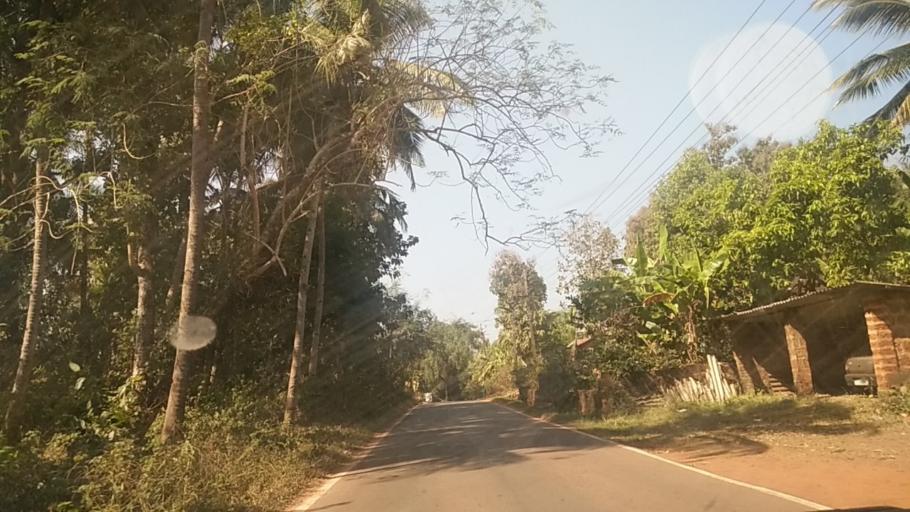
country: IN
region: Goa
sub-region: South Goa
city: Curchorem
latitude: 15.2857
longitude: 74.0785
